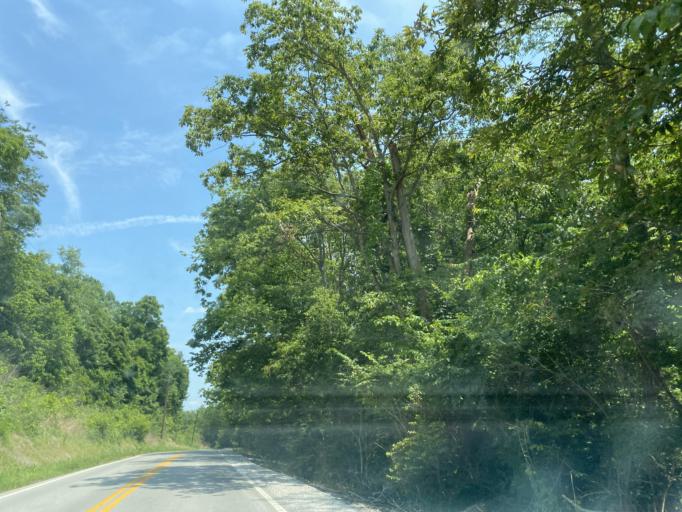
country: US
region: Kentucky
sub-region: Campbell County
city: Claryville
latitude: 38.8928
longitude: -84.4470
